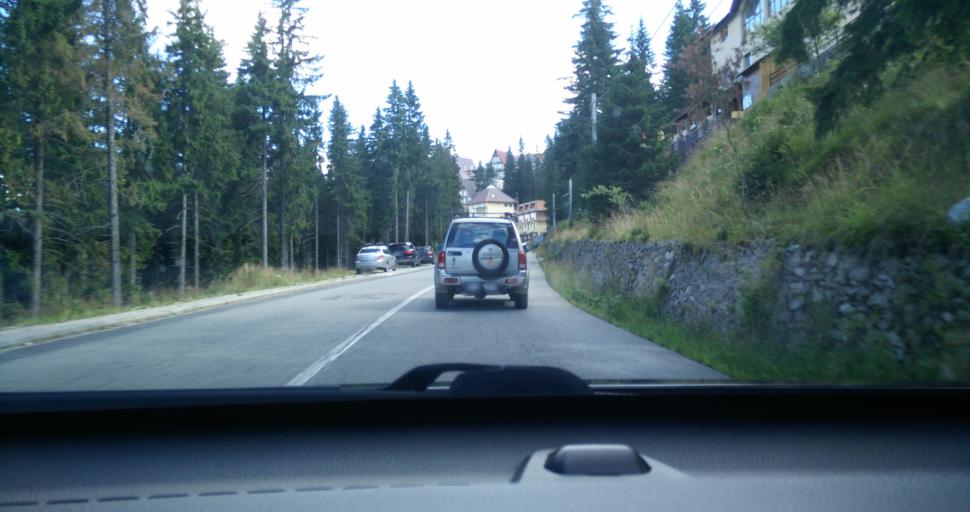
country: RO
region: Gorj
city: Novaci-Straini
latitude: 45.2851
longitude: 23.6916
